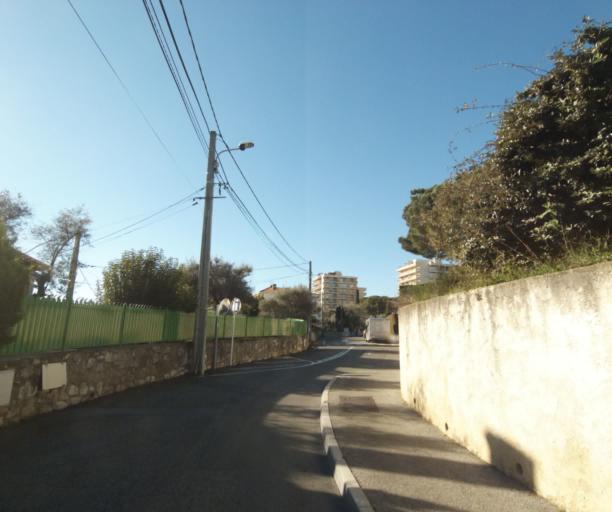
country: FR
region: Provence-Alpes-Cote d'Azur
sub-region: Departement des Alpes-Maritimes
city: Antibes
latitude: 43.5771
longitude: 7.1133
